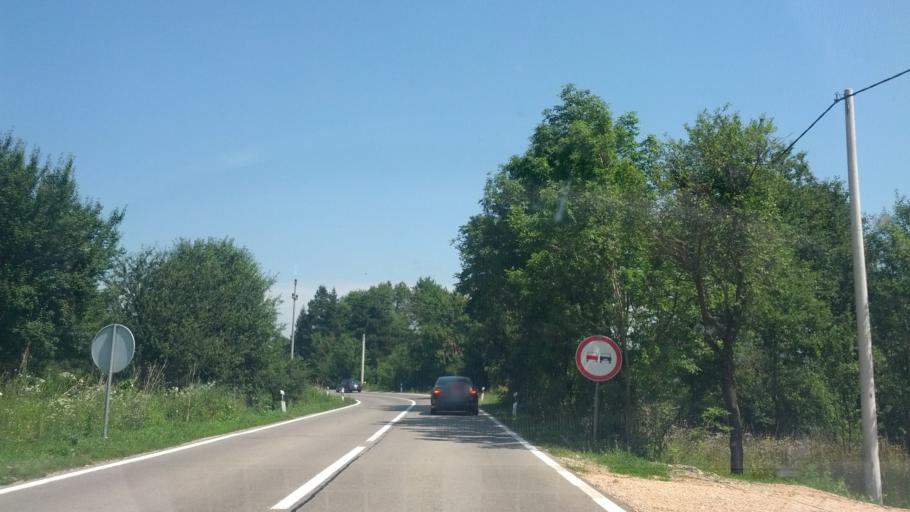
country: BA
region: Federation of Bosnia and Herzegovina
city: Izacic
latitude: 44.8840
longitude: 15.7271
